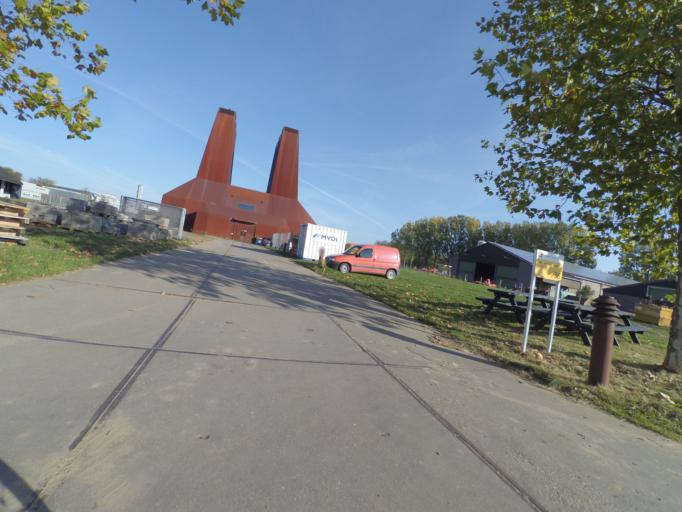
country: NL
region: Utrecht
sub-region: Gemeente Bunnik
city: Bunnik
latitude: 52.0810
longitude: 5.1845
